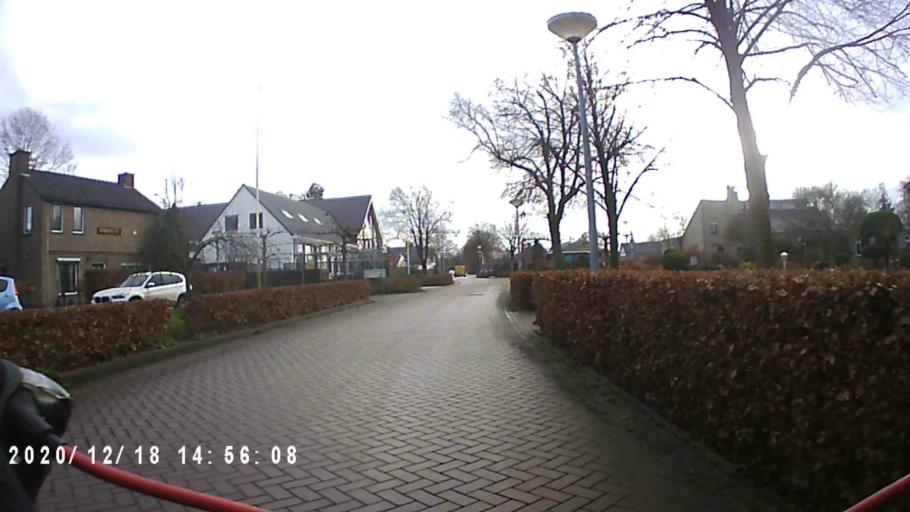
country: NL
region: Groningen
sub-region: Gemeente Haren
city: Haren
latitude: 53.1844
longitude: 6.6860
